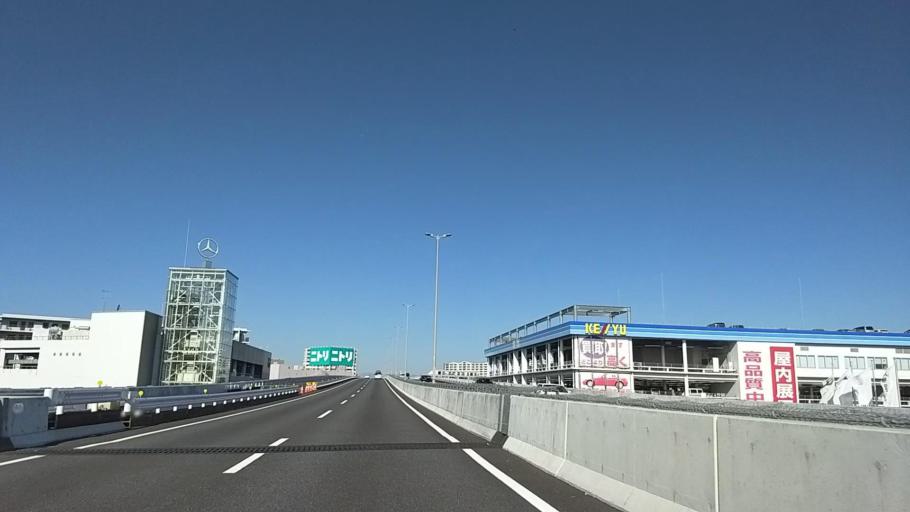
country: JP
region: Kanagawa
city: Minami-rinkan
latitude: 35.5077
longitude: 139.4779
